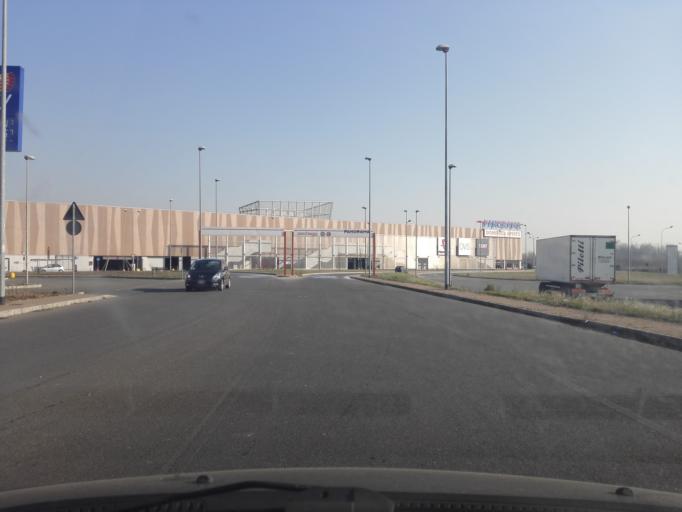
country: IT
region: Piedmont
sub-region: Provincia di Alessandria
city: Alessandria
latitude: 44.9018
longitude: 8.6303
